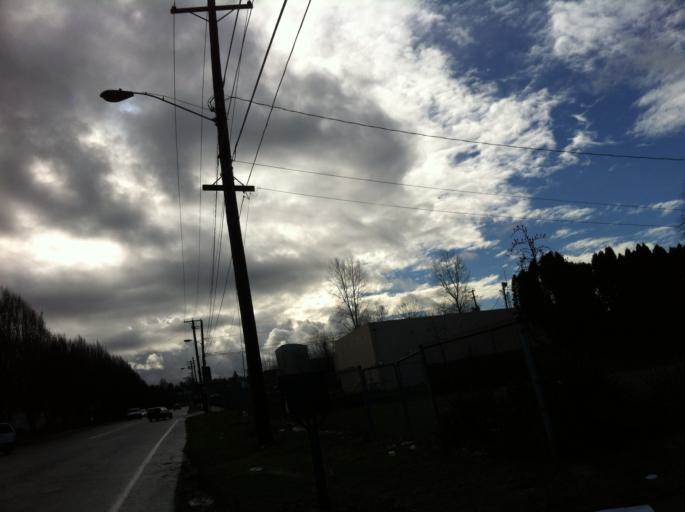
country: US
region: Oregon
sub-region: Multnomah County
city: Lents
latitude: 45.5560
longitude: -122.5383
